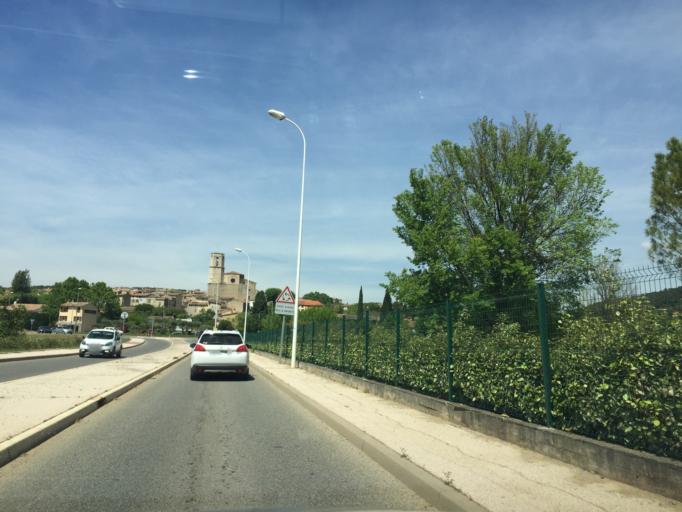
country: FR
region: Provence-Alpes-Cote d'Azur
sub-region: Departement du Var
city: Lorgues
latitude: 43.4890
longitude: 6.3648
